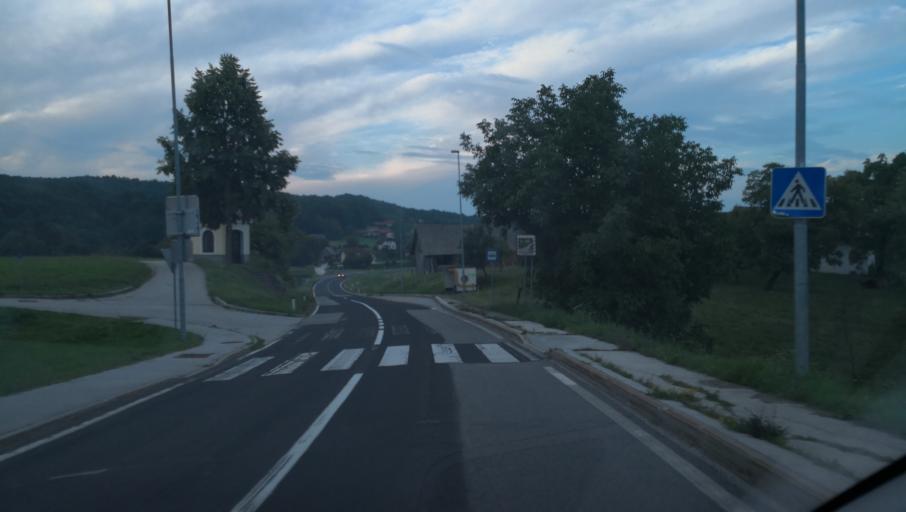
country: SI
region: Metlika
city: Metlika
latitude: 45.6724
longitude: 15.2861
